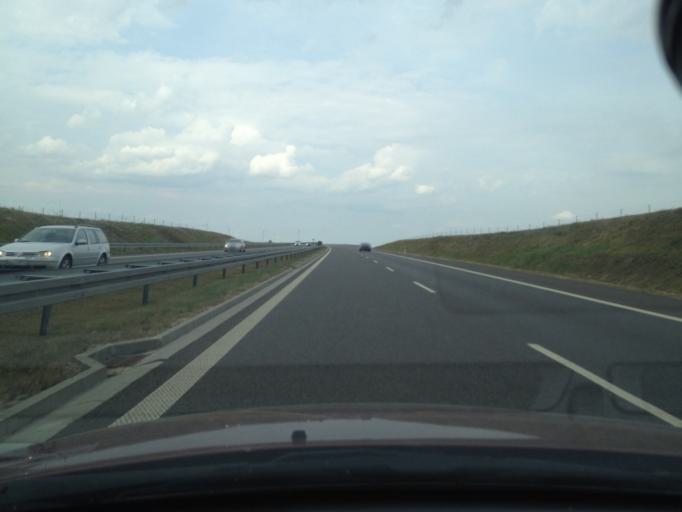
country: PL
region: West Pomeranian Voivodeship
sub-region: Powiat pyrzycki
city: Kozielice
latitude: 53.0673
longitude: 14.8621
